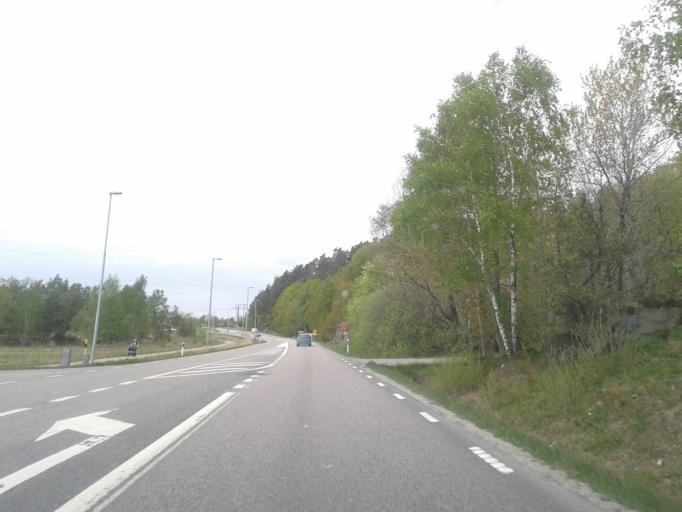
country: SE
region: Vaestra Goetaland
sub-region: Kungalvs Kommun
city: Kungalv
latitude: 57.8691
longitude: 11.9134
